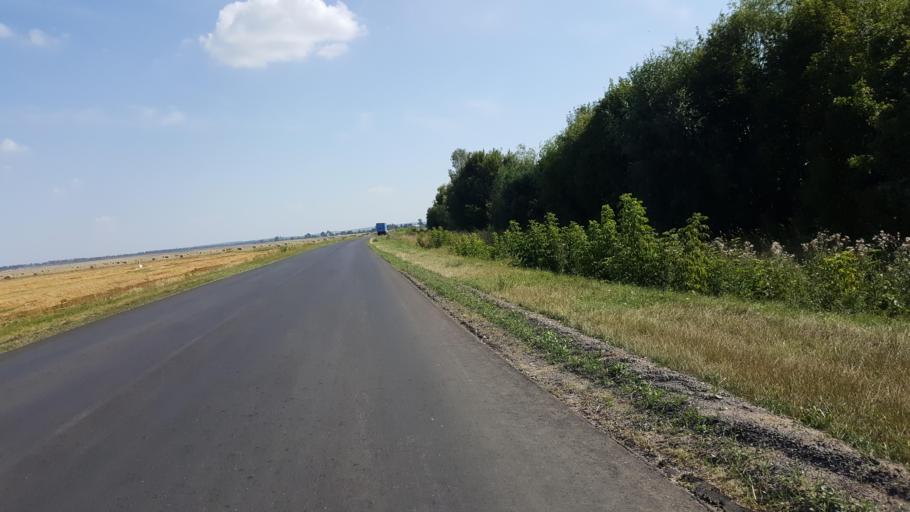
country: BY
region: Brest
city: Kamyanyets
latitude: 52.4426
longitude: 23.7409
